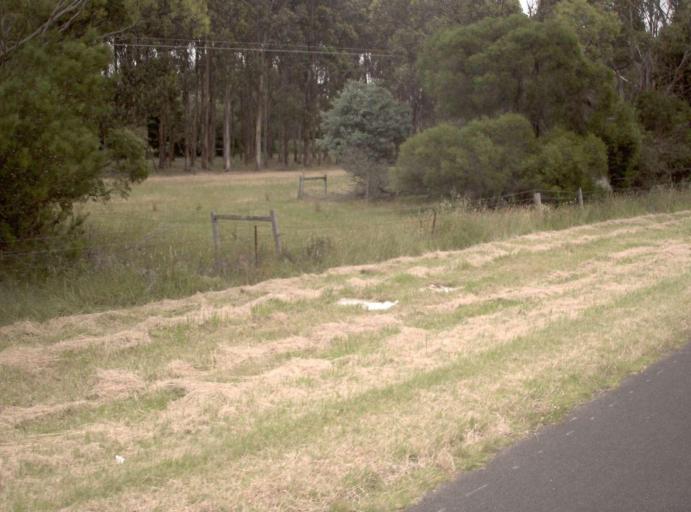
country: AU
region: Victoria
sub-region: Latrobe
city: Morwell
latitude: -38.2728
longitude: 146.4221
